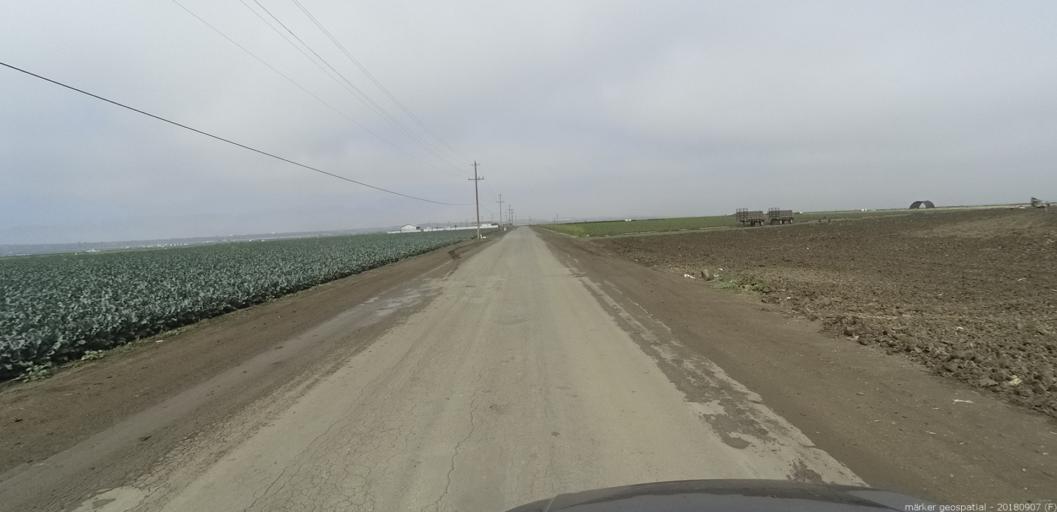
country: US
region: California
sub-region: Monterey County
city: Boronda
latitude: 36.6924
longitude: -121.7099
